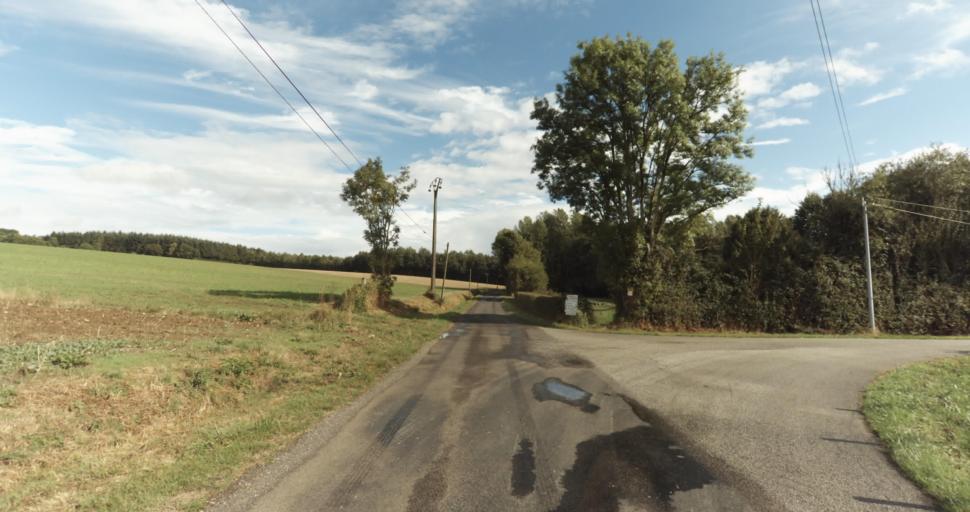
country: FR
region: Lower Normandy
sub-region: Departement de l'Orne
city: Sainte-Gauburge-Sainte-Colombe
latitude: 48.6945
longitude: 0.3782
